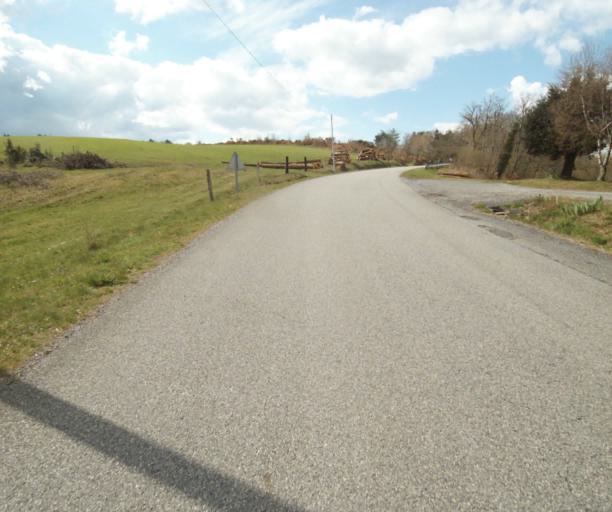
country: FR
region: Limousin
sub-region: Departement de la Correze
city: Correze
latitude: 45.3035
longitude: 1.8909
